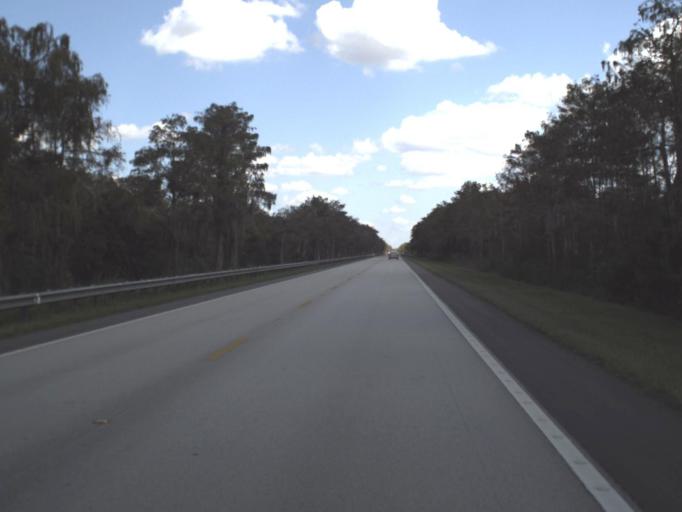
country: US
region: Florida
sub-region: Miami-Dade County
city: Kendall West
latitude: 25.8479
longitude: -80.9451
